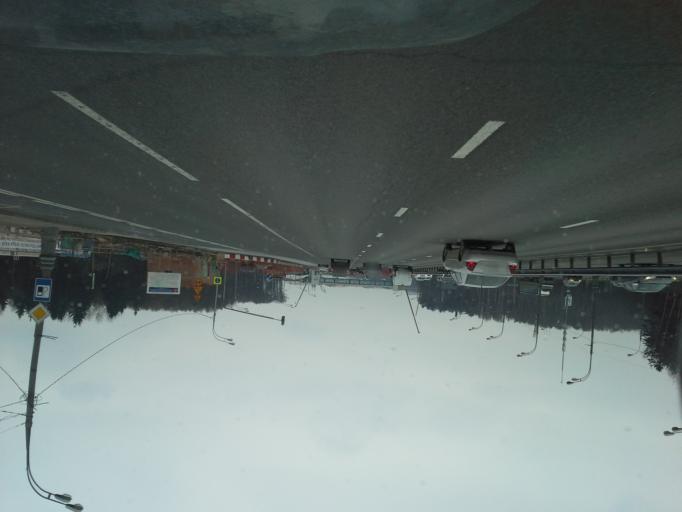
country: RU
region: Moscow
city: Troparevo
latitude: 55.6433
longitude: 37.4688
